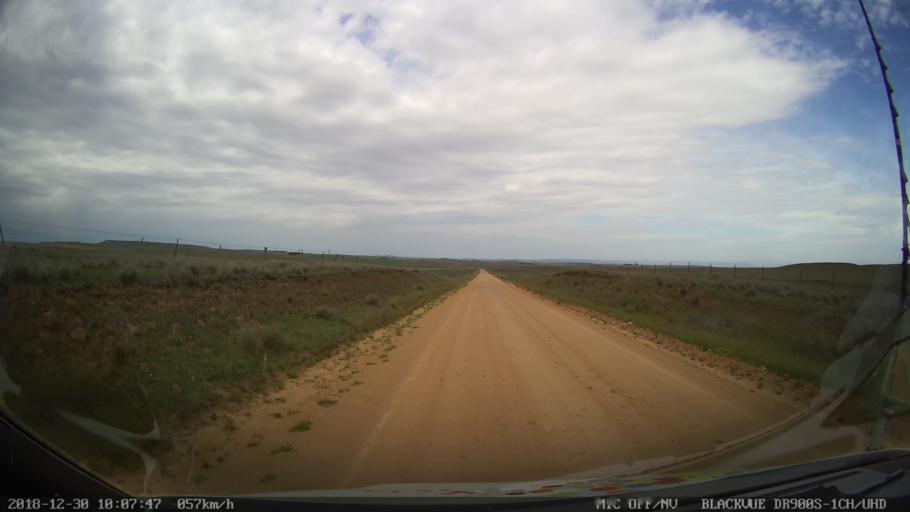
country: AU
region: New South Wales
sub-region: Cooma-Monaro
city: Cooma
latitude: -36.5415
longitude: 149.1198
